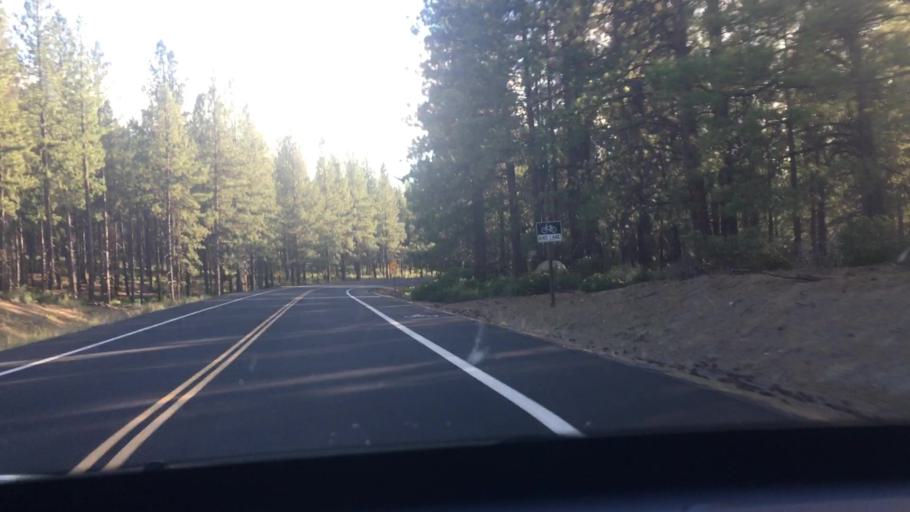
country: US
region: Oregon
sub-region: Deschutes County
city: Deschutes River Woods
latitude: 44.0389
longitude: -121.4198
